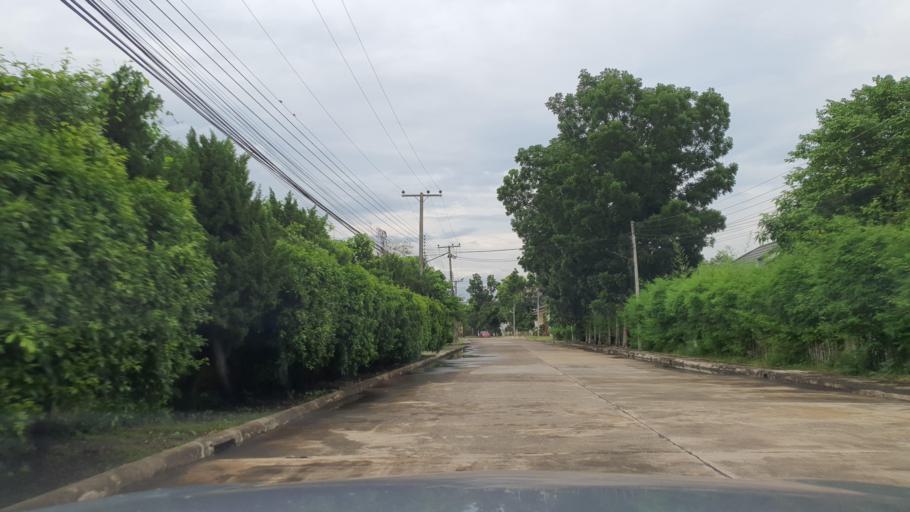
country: TH
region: Chiang Mai
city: San Kamphaeng
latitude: 18.7745
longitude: 99.0707
